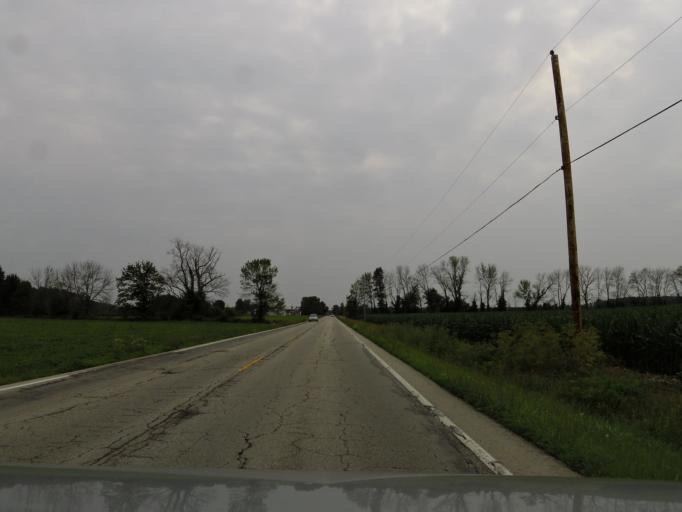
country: US
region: Ohio
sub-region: Clinton County
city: Blanchester
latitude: 39.3202
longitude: -83.9030
